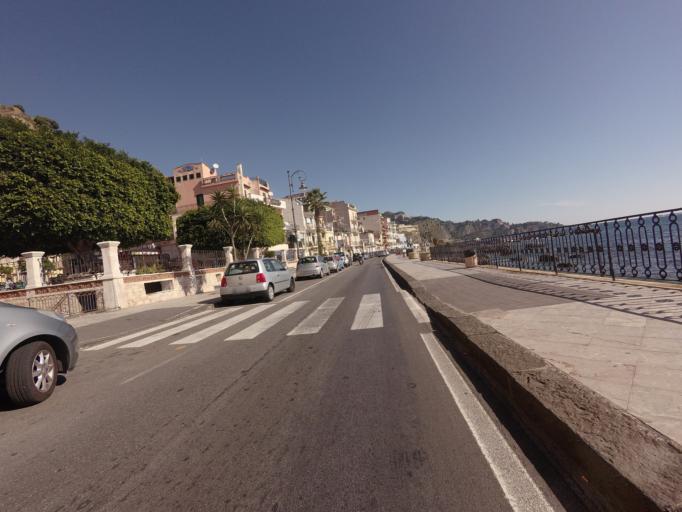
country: IT
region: Sicily
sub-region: Messina
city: Giardini-Naxos
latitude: 37.8402
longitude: 15.2774
